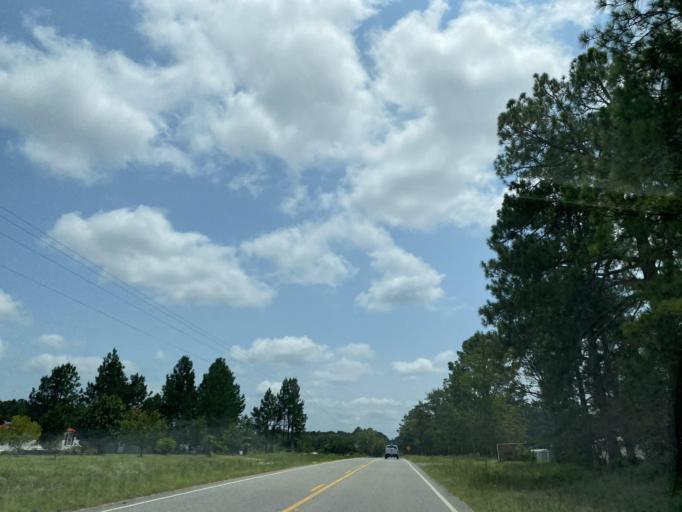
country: US
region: Georgia
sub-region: Jeff Davis County
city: Hazlehurst
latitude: 31.7833
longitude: -82.5636
